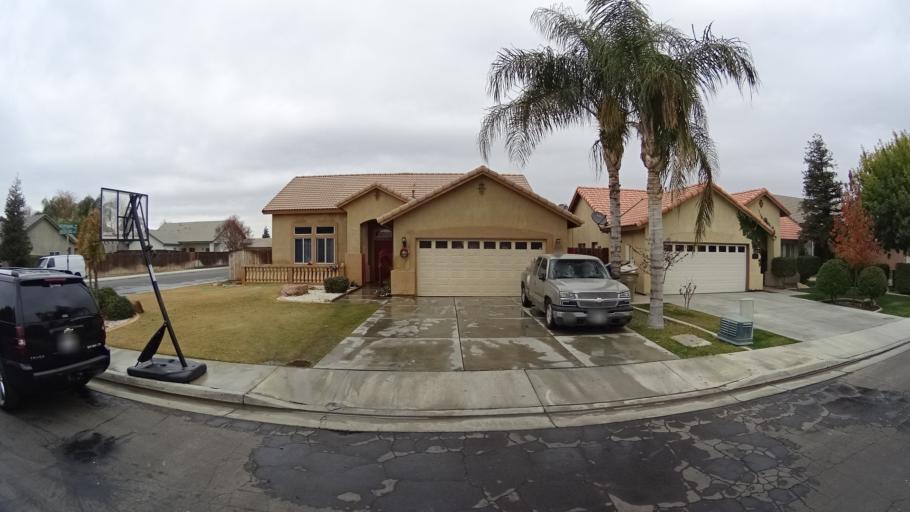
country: US
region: California
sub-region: Kern County
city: Greenfield
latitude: 35.2853
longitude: -119.0332
